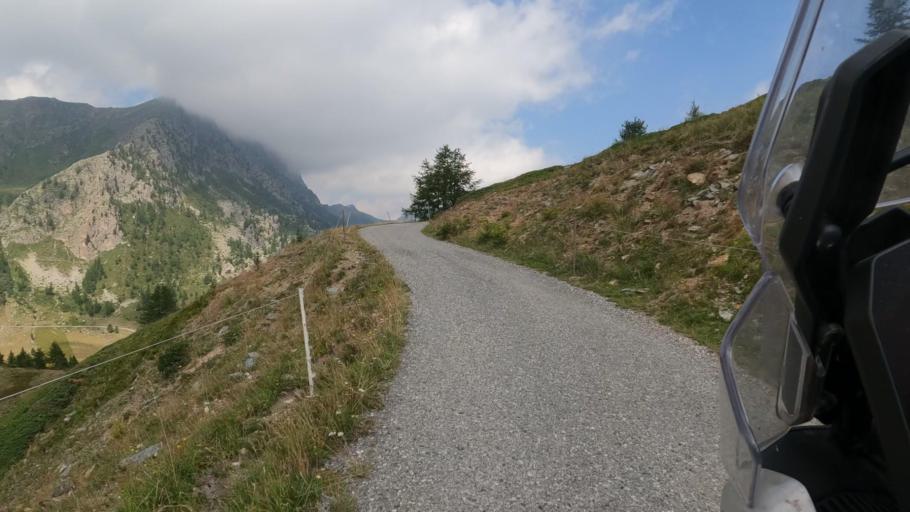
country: IT
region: Piedmont
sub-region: Provincia di Cuneo
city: Marmora
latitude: 44.4029
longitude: 7.1136
